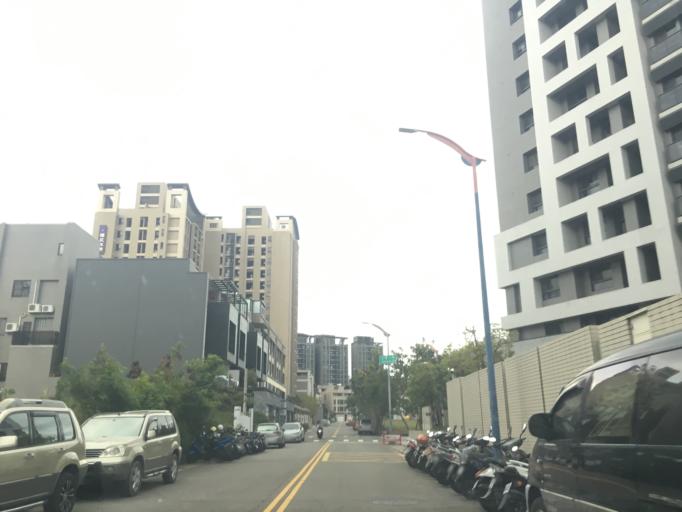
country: TW
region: Taiwan
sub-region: Taichung City
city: Taichung
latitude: 24.1592
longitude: 120.7216
